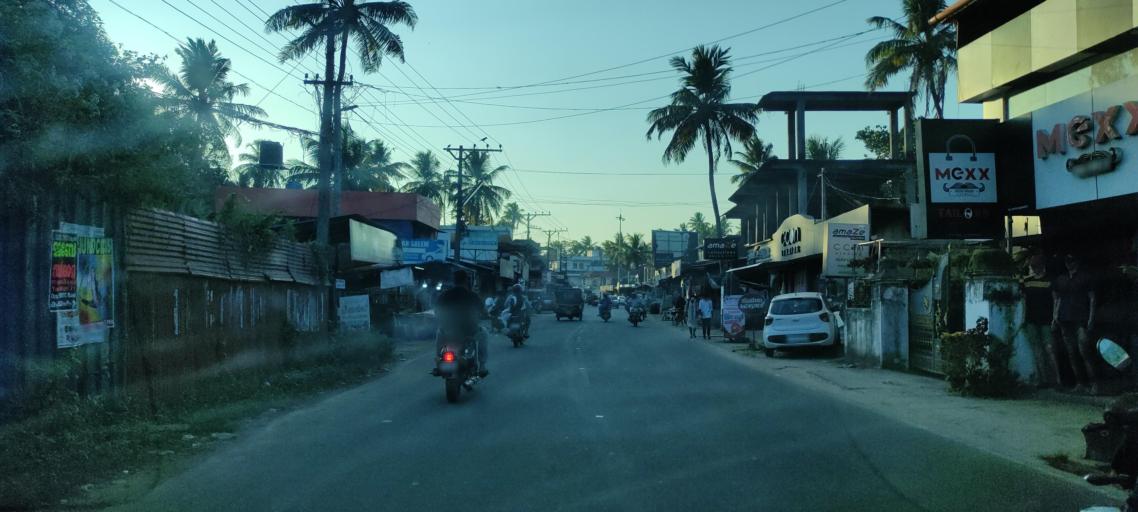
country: IN
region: Kerala
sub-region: Alappuzha
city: Kayankulam
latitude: 9.1773
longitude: 76.4876
